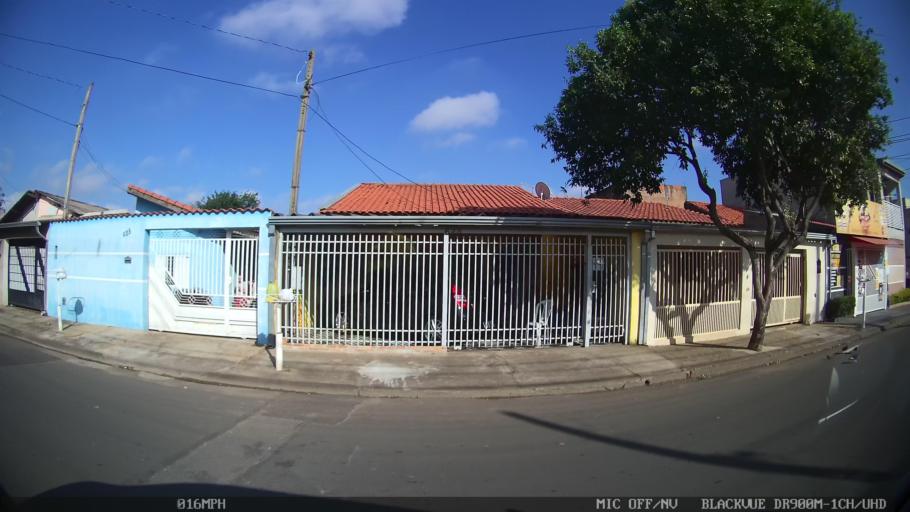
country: BR
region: Sao Paulo
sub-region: Hortolandia
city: Hortolandia
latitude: -22.8987
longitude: -47.1771
